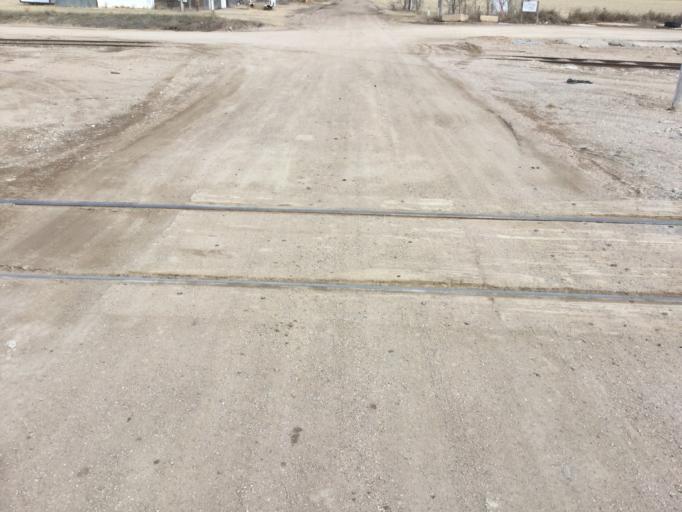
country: US
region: Kansas
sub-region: Lane County
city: Dighton
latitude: 38.4862
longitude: -100.4617
